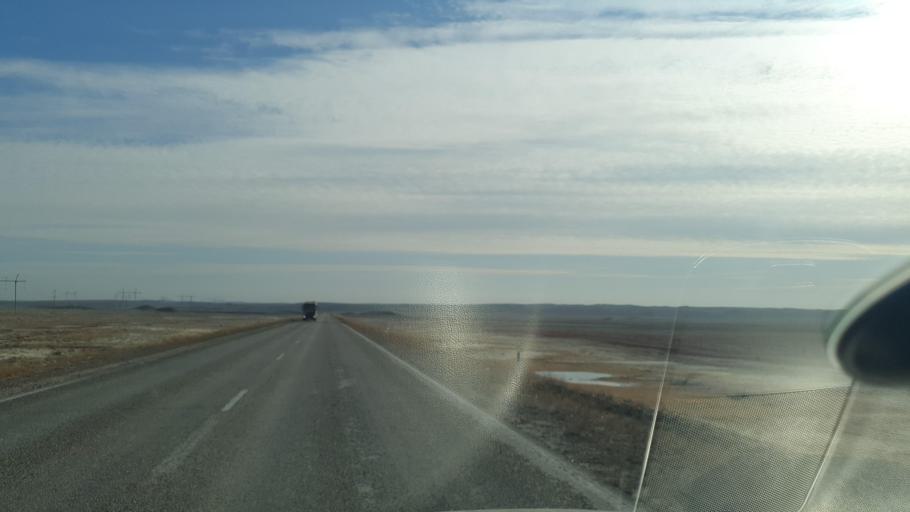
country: KZ
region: Zhambyl
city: Mynaral
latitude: 45.5736
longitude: 73.4146
